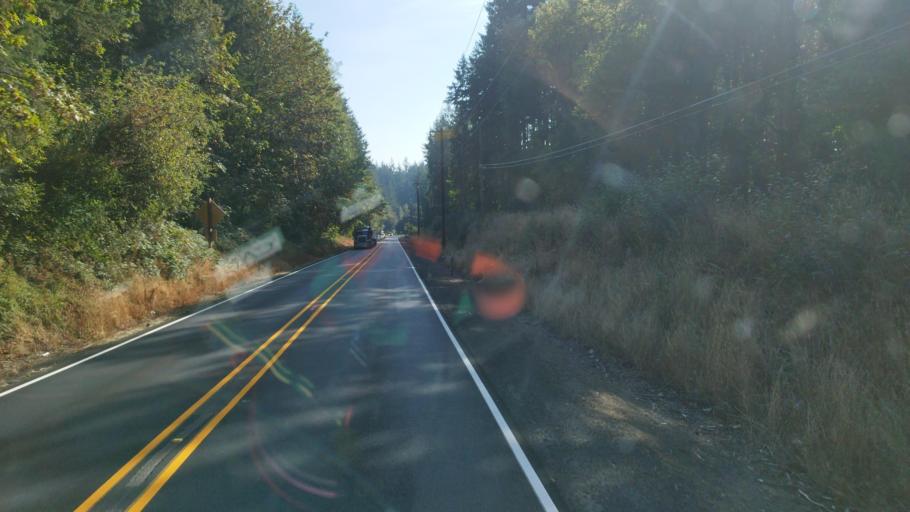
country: US
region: Oregon
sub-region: Washington County
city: Bethany
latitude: 45.6040
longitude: -122.8603
